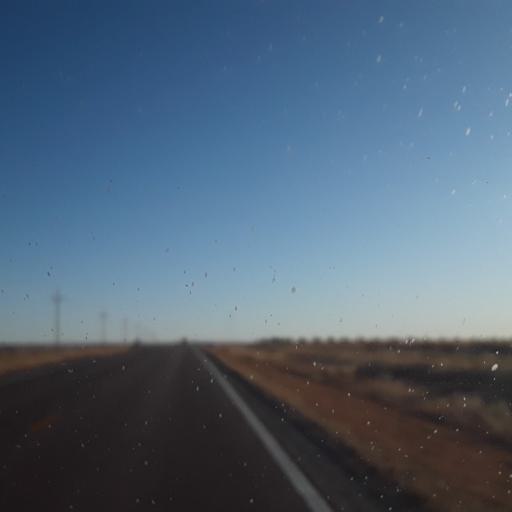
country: US
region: Kansas
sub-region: Wallace County
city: Sharon Springs
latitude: 38.9214
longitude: -101.7495
